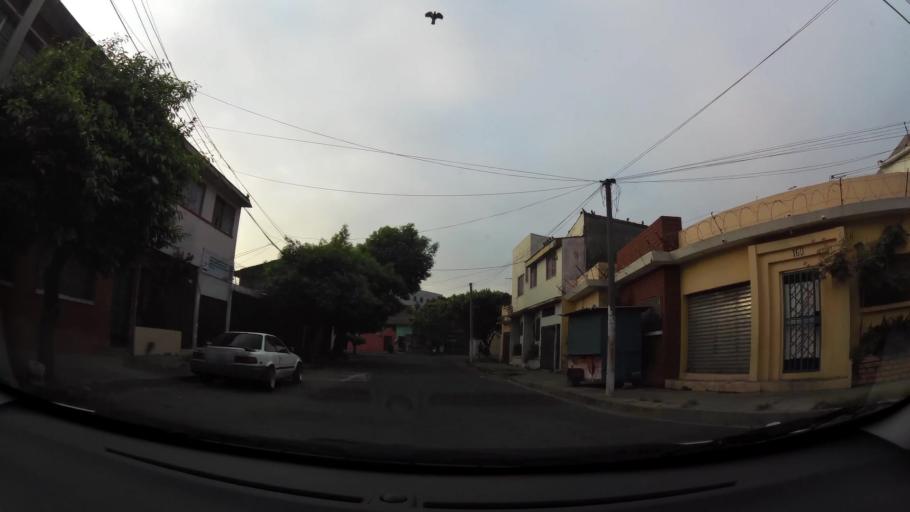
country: SV
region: San Salvador
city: San Salvador
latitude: 13.7064
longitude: -89.1878
